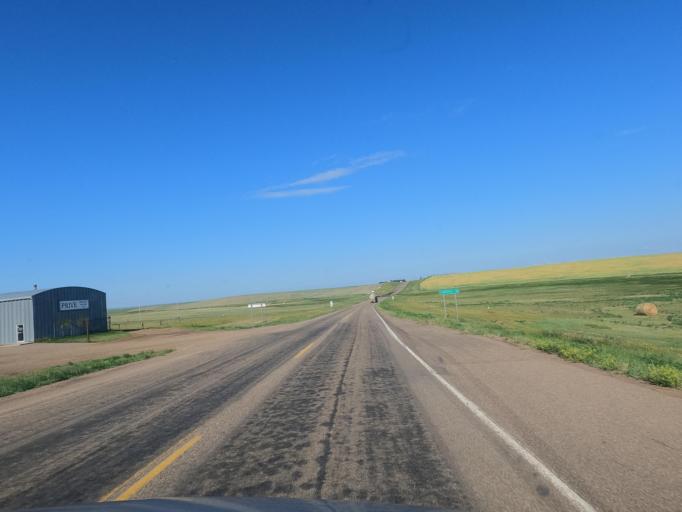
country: CA
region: Saskatchewan
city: Swift Current
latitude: 49.7279
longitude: -107.4971
